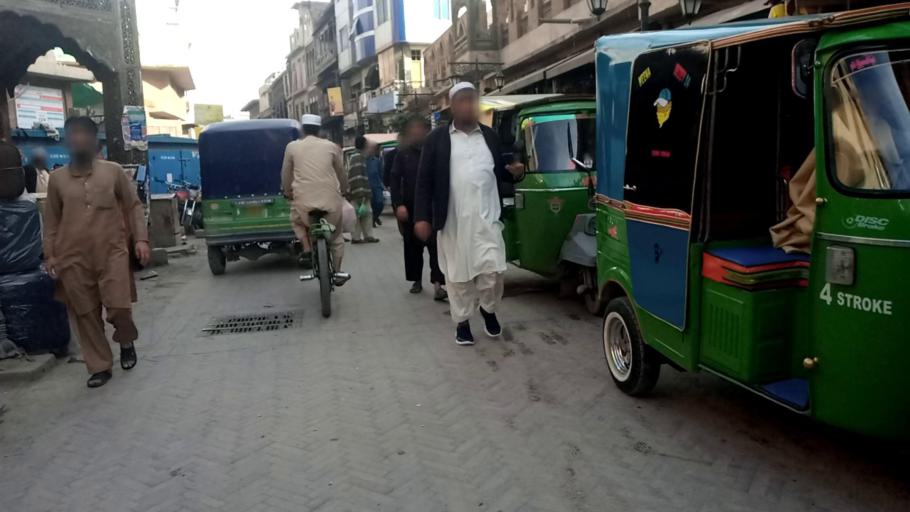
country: PK
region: Khyber Pakhtunkhwa
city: Peshawar
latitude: 34.0093
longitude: 71.5766
